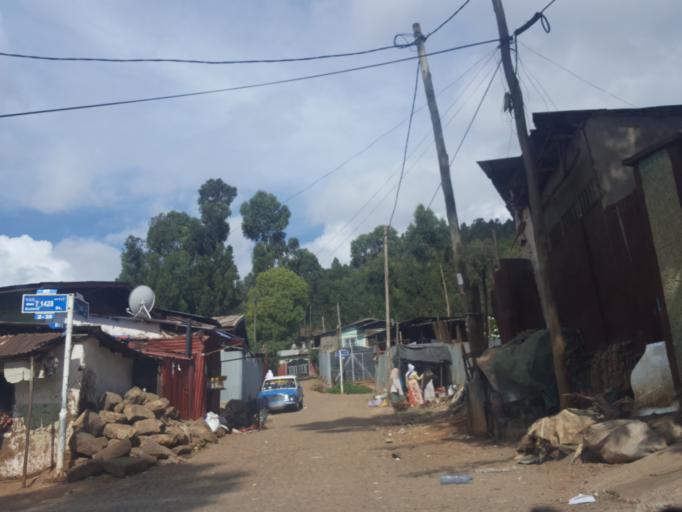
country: ET
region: Adis Abeba
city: Addis Ababa
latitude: 9.0666
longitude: 38.7473
